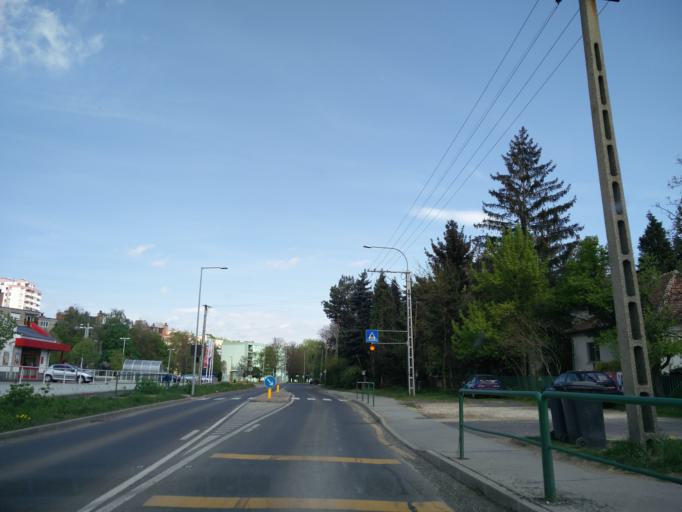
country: HU
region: Zala
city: Zalaegerszeg
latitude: 46.8313
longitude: 16.8280
